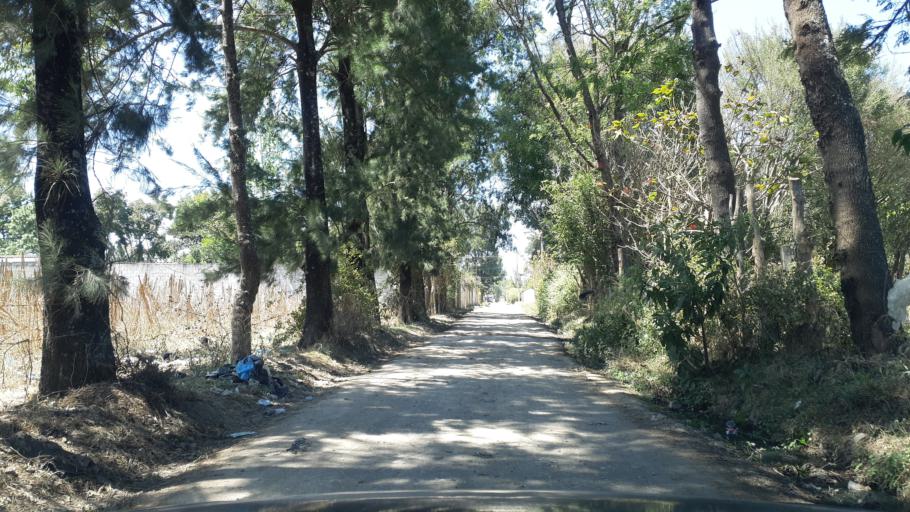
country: GT
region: Chimaltenango
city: El Tejar
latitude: 14.6504
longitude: -90.8070
